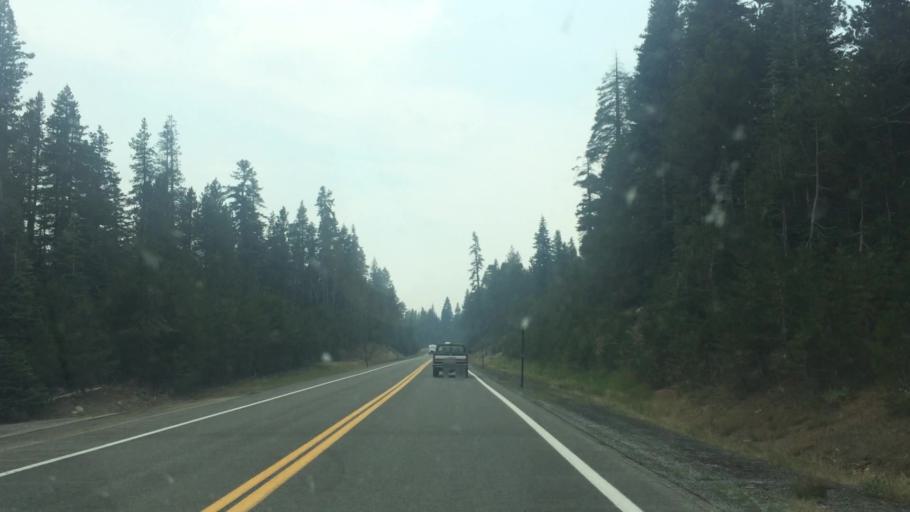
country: US
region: California
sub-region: Calaveras County
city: Arnold
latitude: 38.6160
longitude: -120.2212
